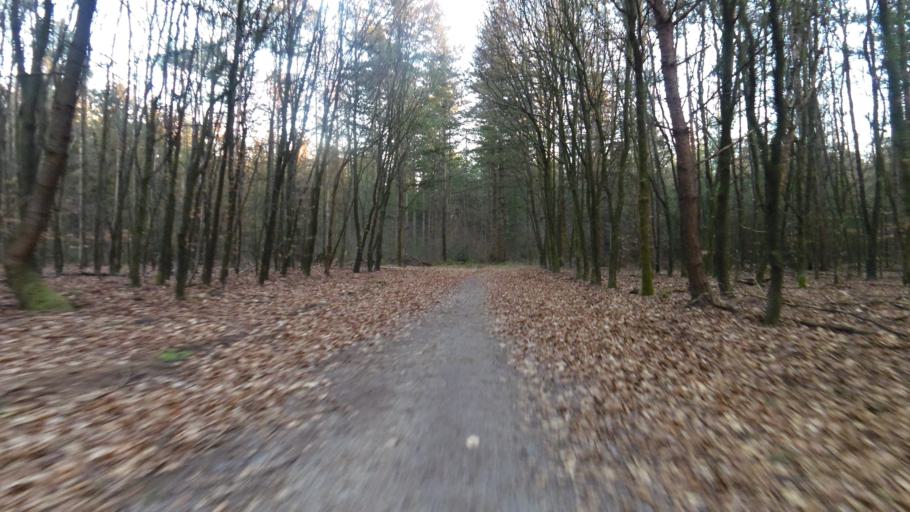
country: NL
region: Gelderland
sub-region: Gemeente Barneveld
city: Garderen
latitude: 52.2335
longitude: 5.6806
